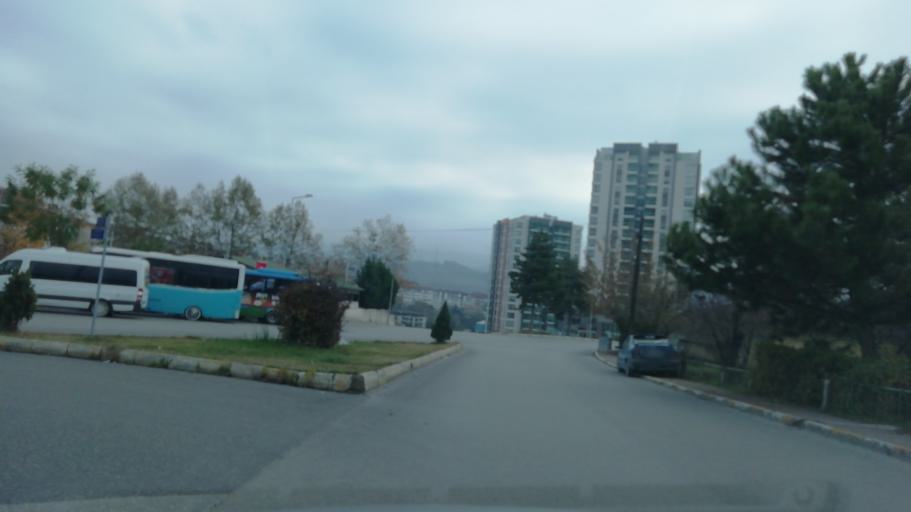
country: TR
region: Karabuk
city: Karabuk
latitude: 41.2068
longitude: 32.6192
